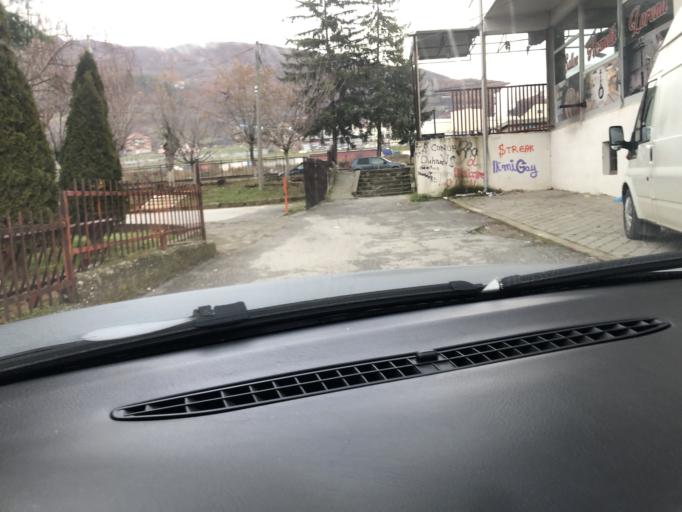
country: MK
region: Debar
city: Debar
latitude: 41.5182
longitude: 20.5295
